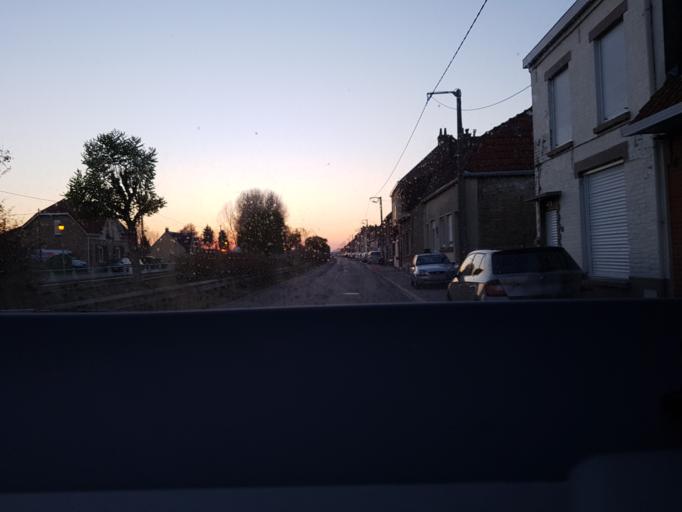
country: FR
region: Nord-Pas-de-Calais
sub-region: Departement du Nord
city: Armbouts-Cappel
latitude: 50.9649
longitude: 2.3439
